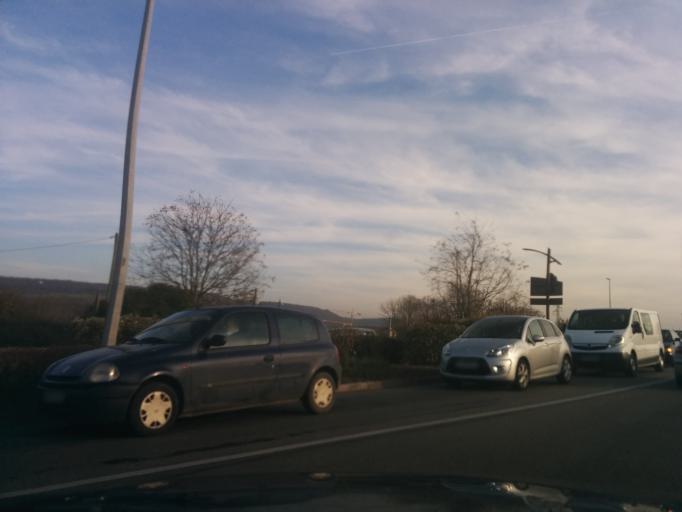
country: FR
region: Haute-Normandie
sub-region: Departement de l'Eure
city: Saint-Marcel
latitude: 49.1057
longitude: 1.4577
